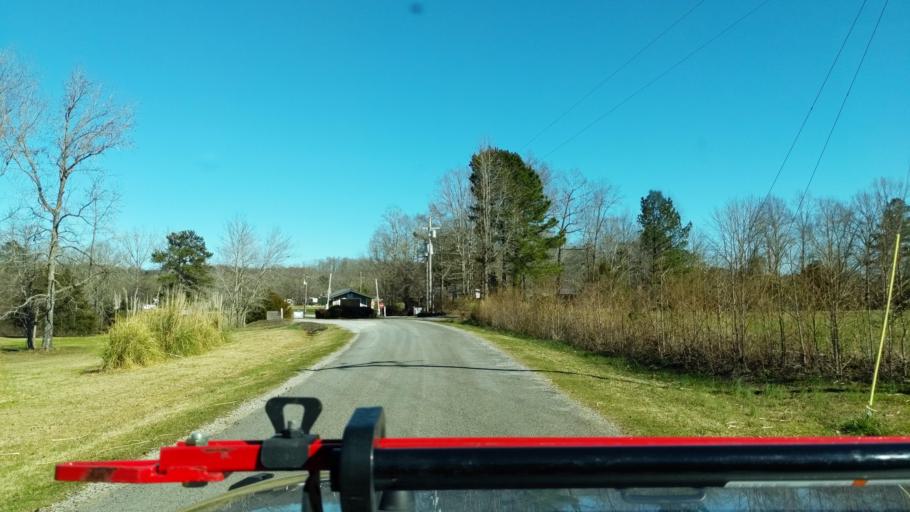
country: US
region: Alabama
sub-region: Walker County
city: Jasper
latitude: 34.0543
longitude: -87.1474
